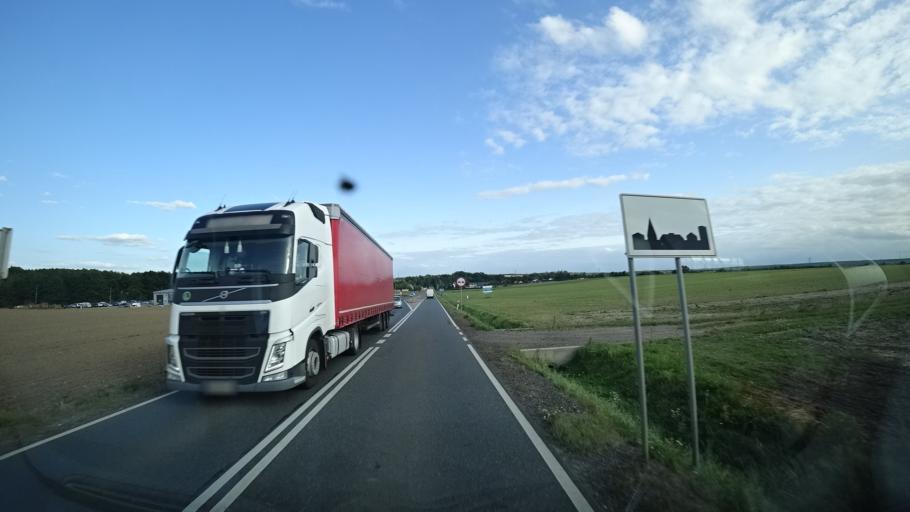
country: PL
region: Silesian Voivodeship
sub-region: Powiat gliwicki
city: Sosnicowice
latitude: 50.2778
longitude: 18.5155
